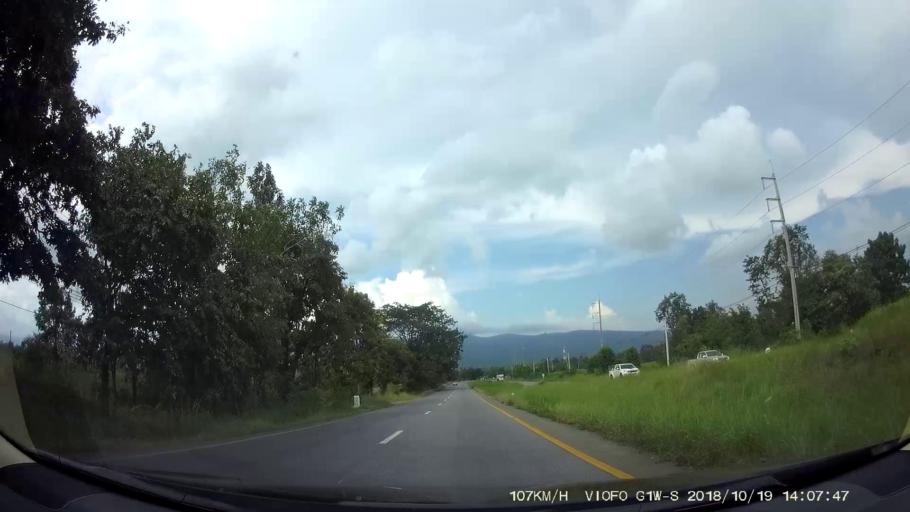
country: TH
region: Chaiyaphum
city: Chaiyaphum
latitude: 15.8985
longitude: 102.1191
